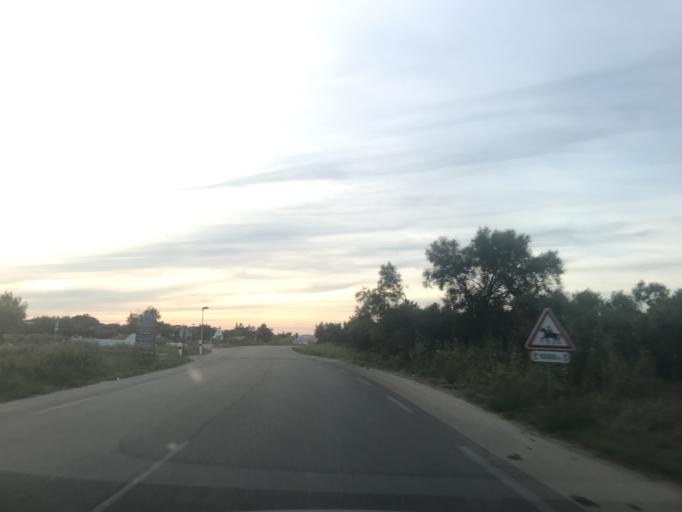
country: FR
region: Provence-Alpes-Cote d'Azur
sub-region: Departement des Bouches-du-Rhone
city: Saintes-Maries-de-la-Mer
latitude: 43.4668
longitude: 4.4181
